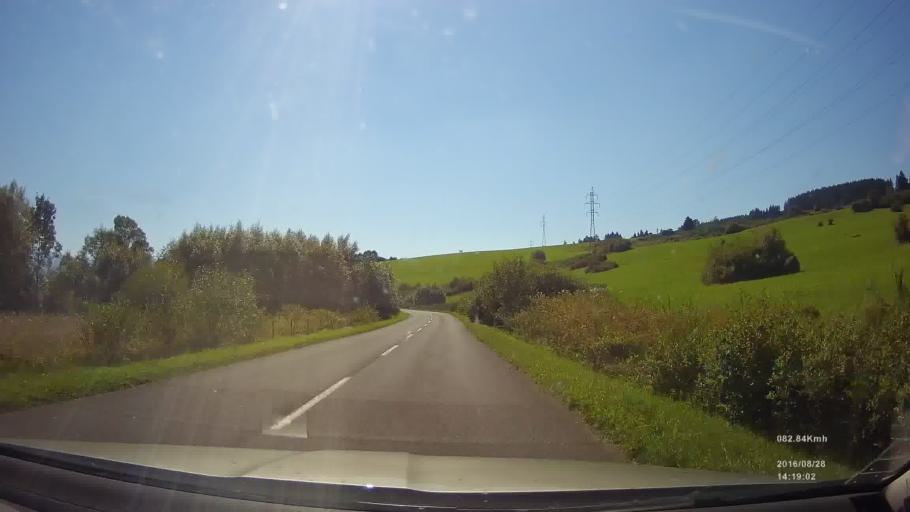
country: SK
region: Zilinsky
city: Ruzomberok
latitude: 49.1167
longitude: 19.4475
